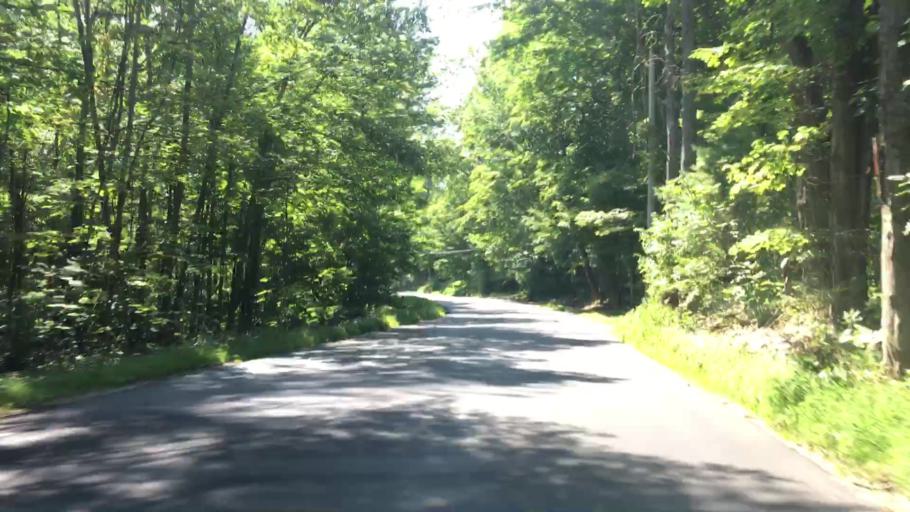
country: US
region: New Hampshire
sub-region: Rockingham County
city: Hampstead
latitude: 42.8771
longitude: -71.2184
